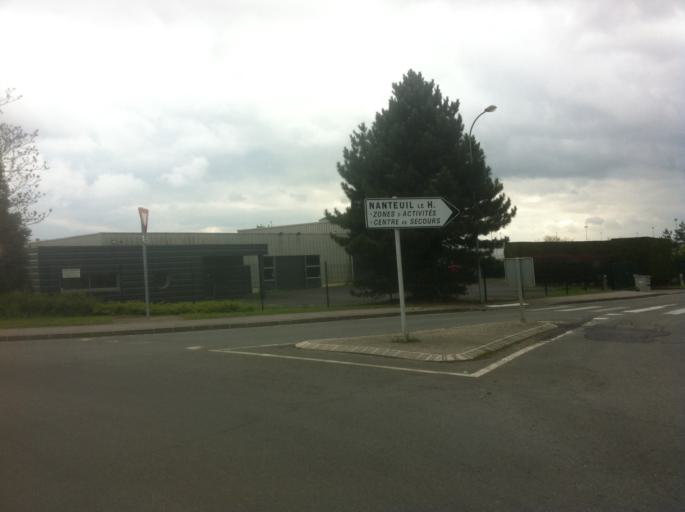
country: FR
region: Picardie
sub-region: Departement de l'Oise
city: Nanteuil-le-Haudouin
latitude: 49.1410
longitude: 2.7977
